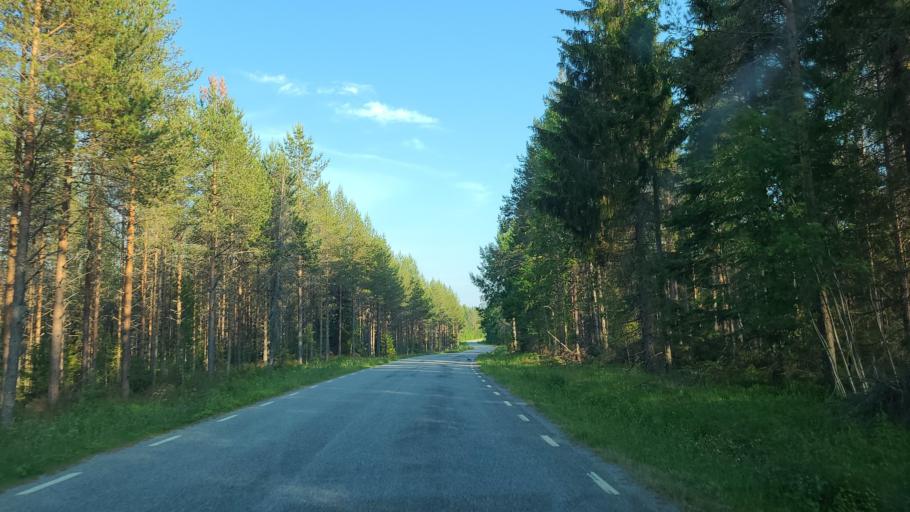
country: SE
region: Vaesterbotten
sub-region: Skelleftea Kommun
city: Burea
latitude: 64.3615
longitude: 21.3336
